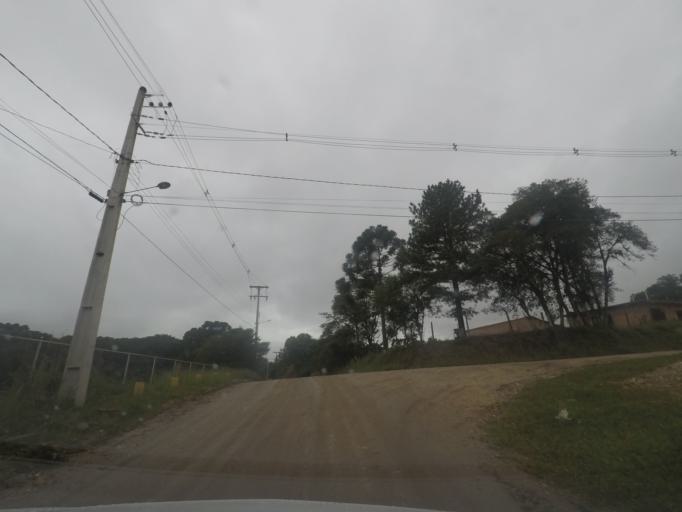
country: BR
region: Parana
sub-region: Campina Grande Do Sul
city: Campina Grande do Sul
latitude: -25.3056
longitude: -49.1107
